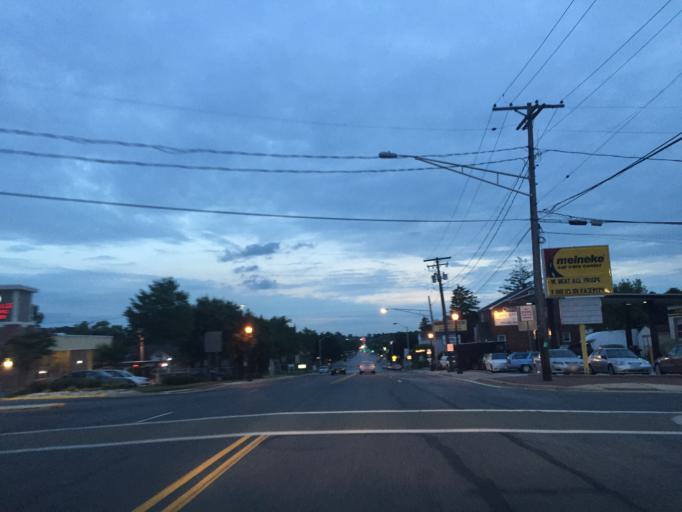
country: US
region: Maryland
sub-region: Baltimore County
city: Parkville
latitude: 39.3727
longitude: -76.5438
